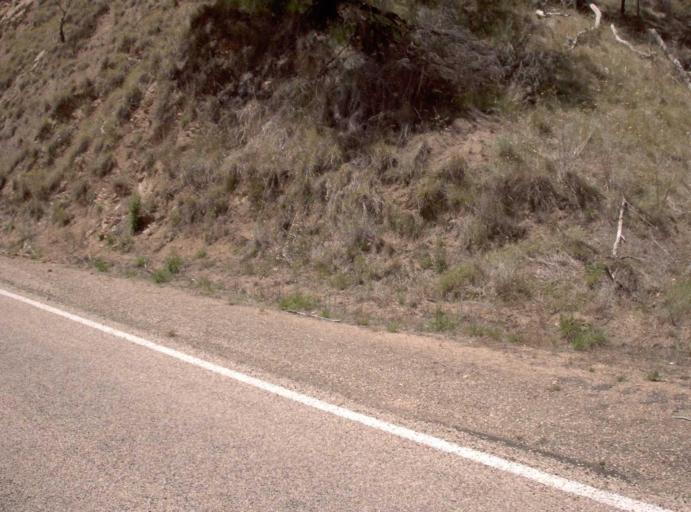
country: AU
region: Victoria
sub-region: Alpine
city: Mount Beauty
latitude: -37.1655
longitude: 147.6598
